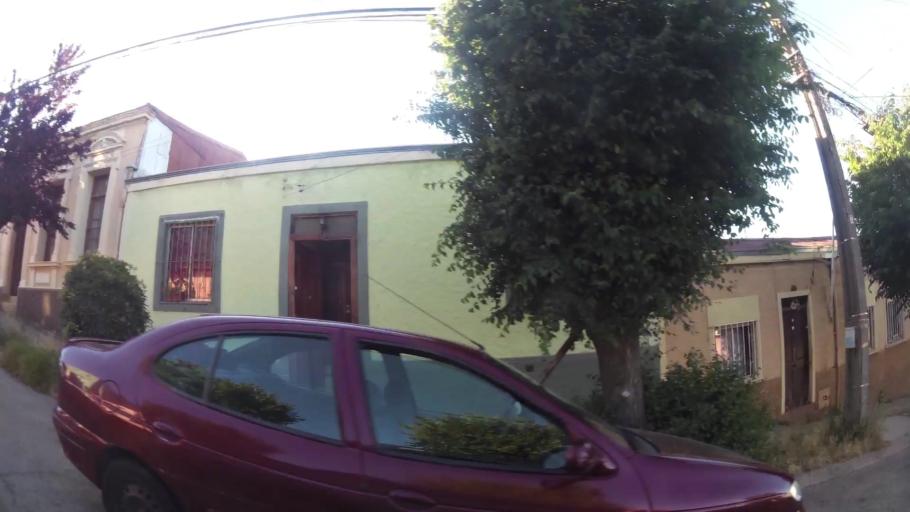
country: CL
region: Valparaiso
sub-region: Provincia de Valparaiso
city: Valparaiso
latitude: -33.0519
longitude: -71.6206
